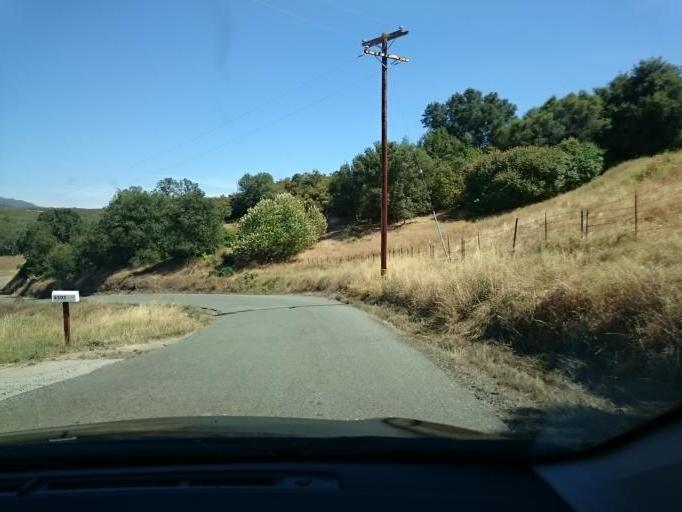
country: US
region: California
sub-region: Calaveras County
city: Rancho Calaveras
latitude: 38.1200
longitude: -120.8025
